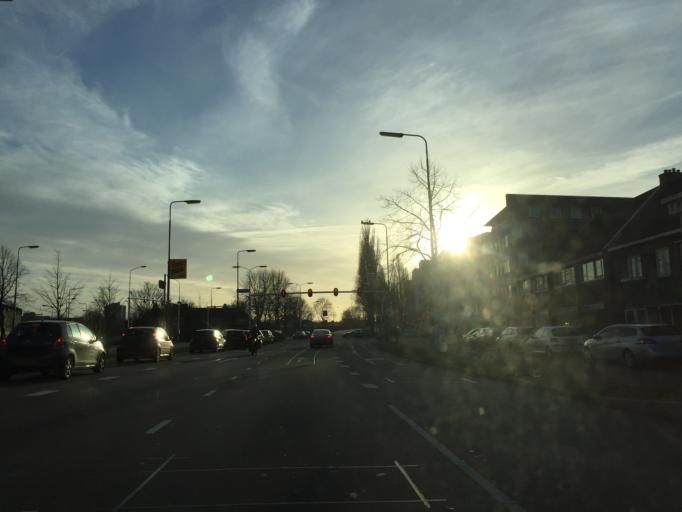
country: NL
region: North Brabant
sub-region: Gemeente 's-Hertogenbosch
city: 's-Hertogenbosch
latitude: 51.6988
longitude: 5.3040
